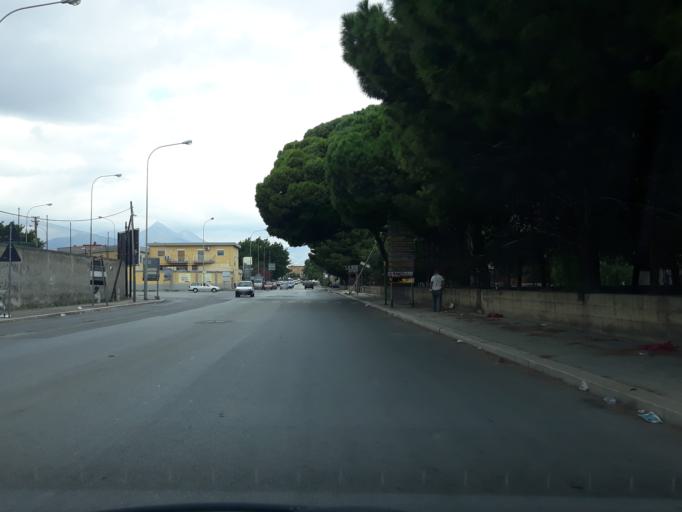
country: IT
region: Sicily
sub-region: Palermo
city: Ciaculli
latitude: 38.0952
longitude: 13.3989
